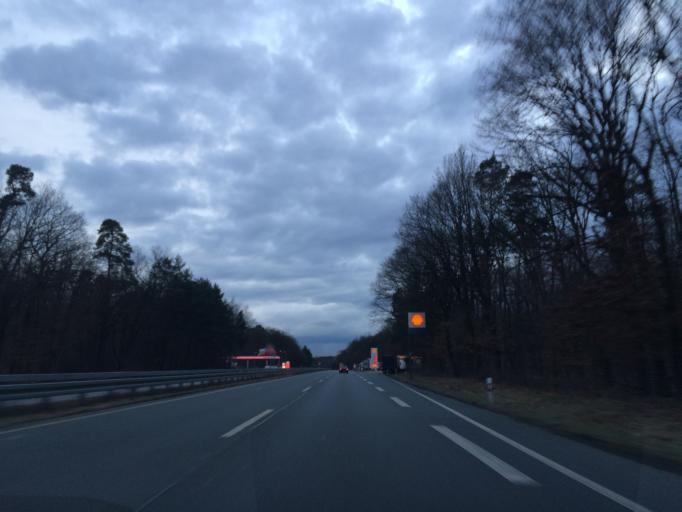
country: DE
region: Hesse
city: Niederrad
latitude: 50.0390
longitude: 8.6272
